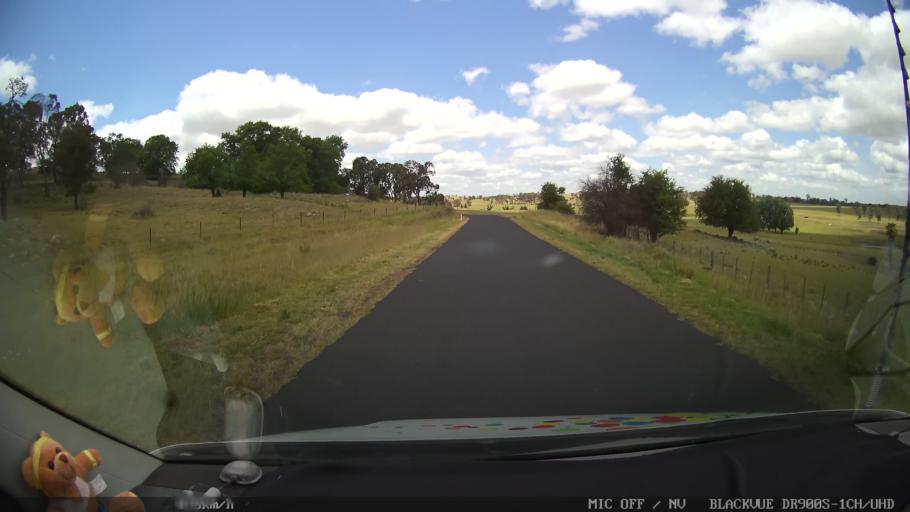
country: AU
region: New South Wales
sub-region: Glen Innes Severn
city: Glen Innes
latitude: -29.4289
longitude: 151.7512
